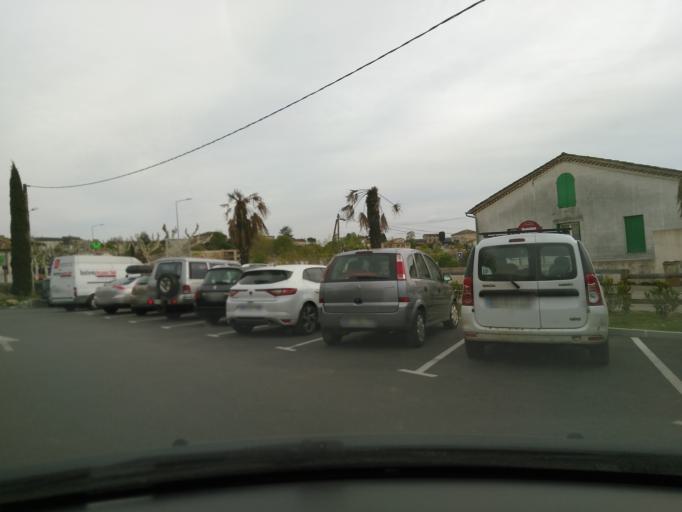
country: FR
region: Rhone-Alpes
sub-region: Departement de l'Ardeche
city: Ruoms
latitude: 44.4070
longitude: 4.3901
